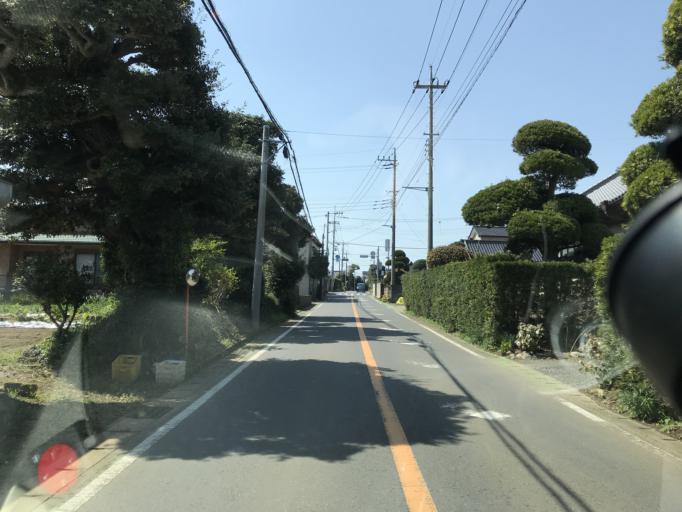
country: JP
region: Chiba
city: Asahi
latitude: 35.7923
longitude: 140.6766
